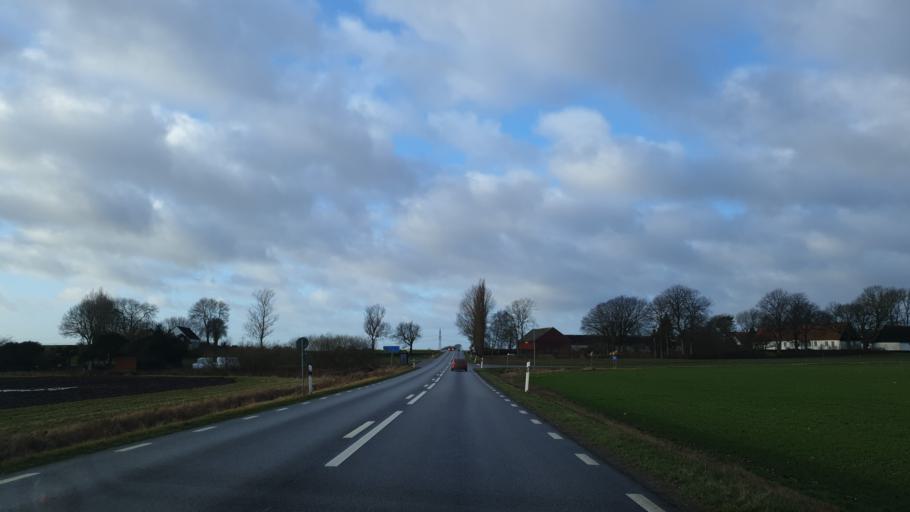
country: SE
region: Skane
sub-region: Svedala Kommun
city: Svedala
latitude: 55.4535
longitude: 13.1815
